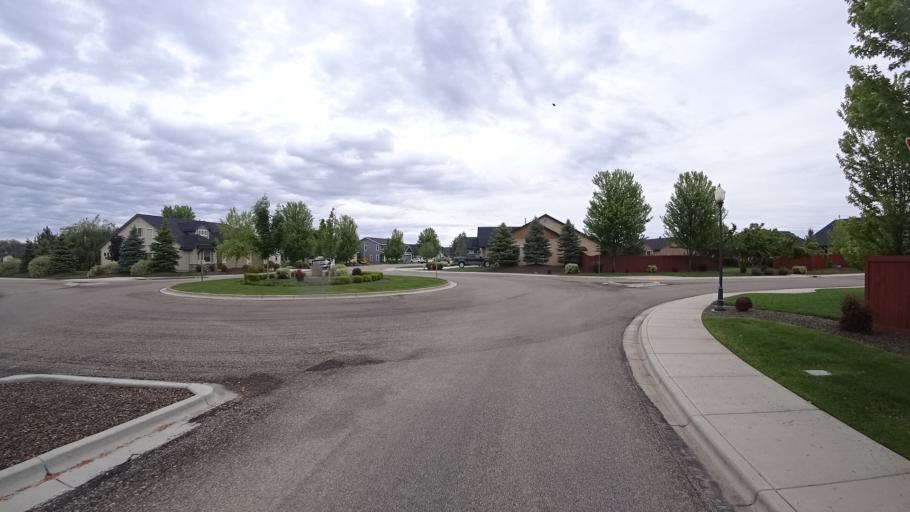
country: US
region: Idaho
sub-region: Ada County
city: Star
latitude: 43.6996
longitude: -116.4812
